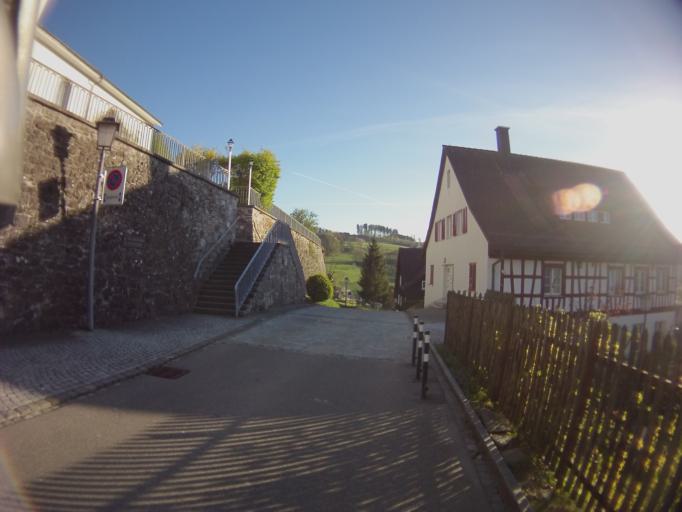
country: CH
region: Zurich
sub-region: Bezirk Dietikon
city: Birmensdorf
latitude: 47.3519
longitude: 8.4411
